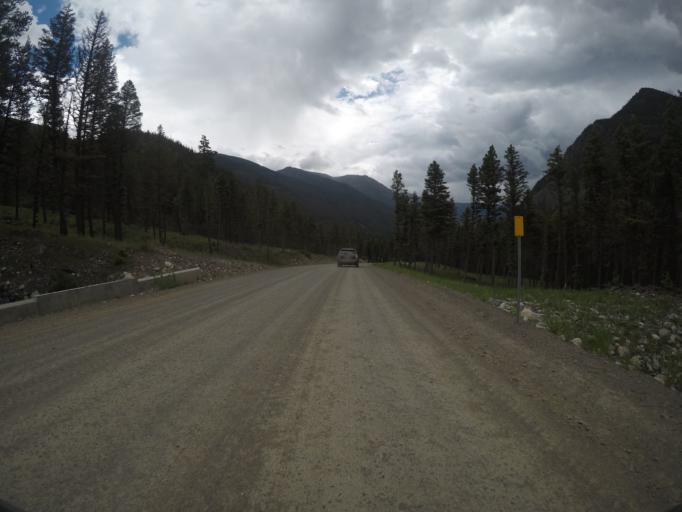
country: US
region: Montana
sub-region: Park County
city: Livingston
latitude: 45.4771
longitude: -110.2065
